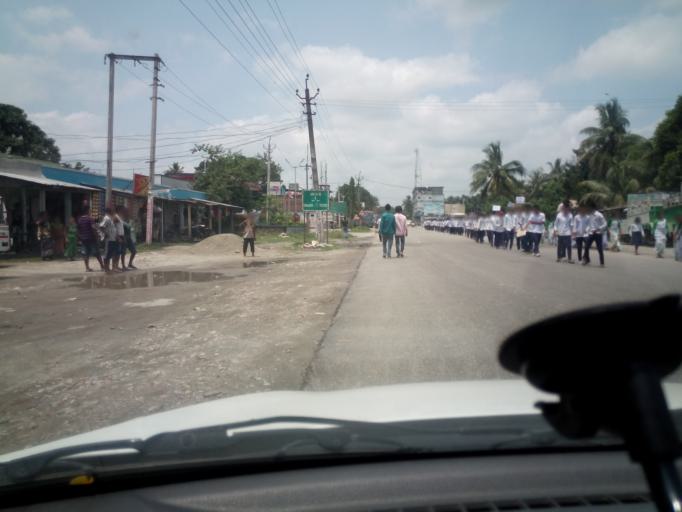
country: IN
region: Assam
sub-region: Udalguri
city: Udalguri
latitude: 26.7100
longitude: 92.2044
